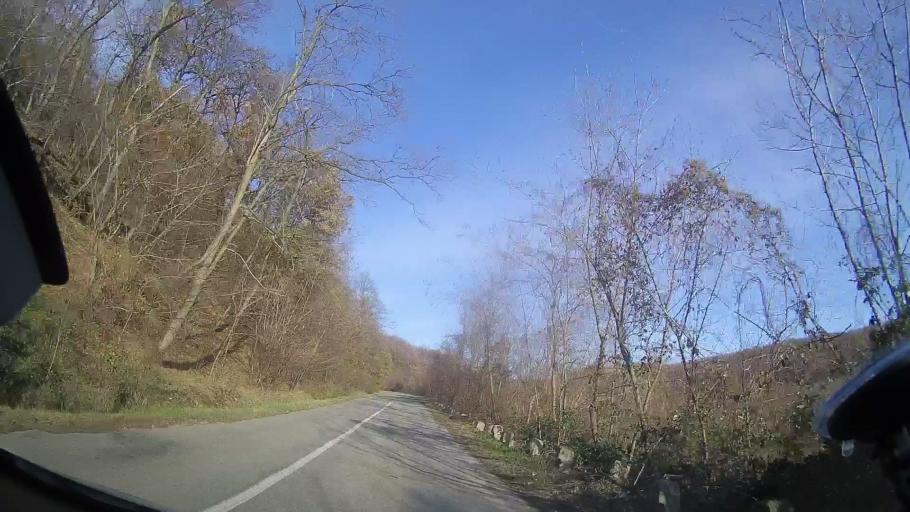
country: RO
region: Bihor
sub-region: Comuna Tileagd
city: Tileagd
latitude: 47.0968
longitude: 22.2406
